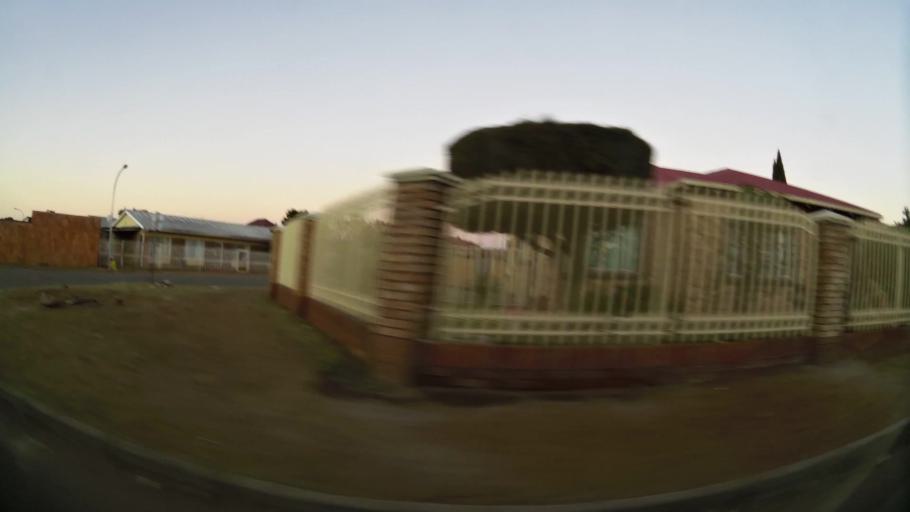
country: ZA
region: Northern Cape
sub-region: Frances Baard District Municipality
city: Kimberley
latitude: -28.7253
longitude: 24.7667
